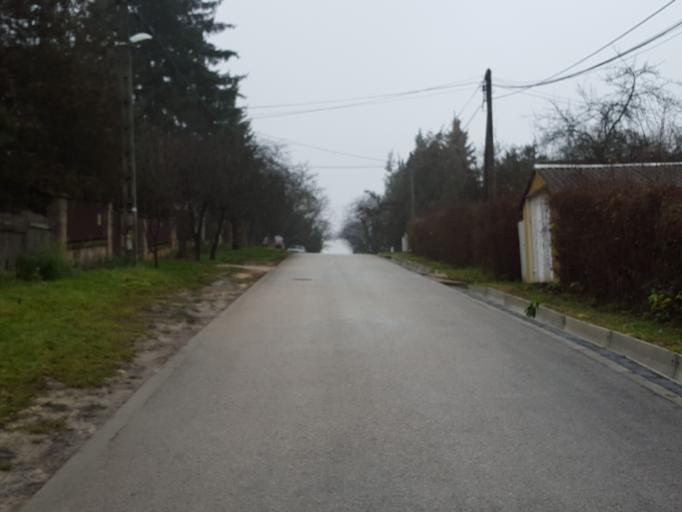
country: HU
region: Pest
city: Budakeszi
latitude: 47.5443
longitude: 18.9494
